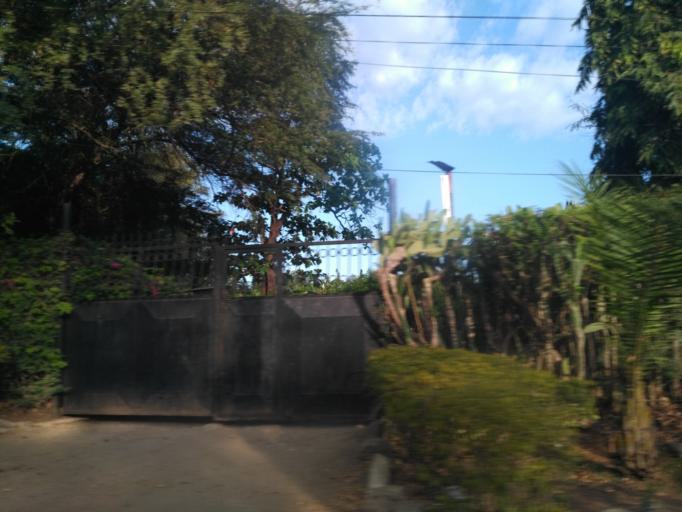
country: TZ
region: Dar es Salaam
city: Magomeni
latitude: -6.7834
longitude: 39.2693
